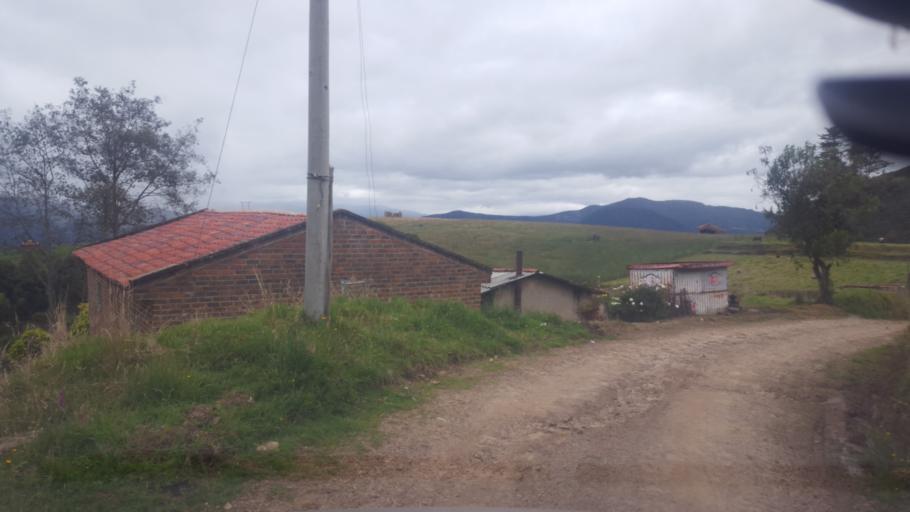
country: CO
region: Boyaca
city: Belen
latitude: 6.0328
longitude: -72.8860
